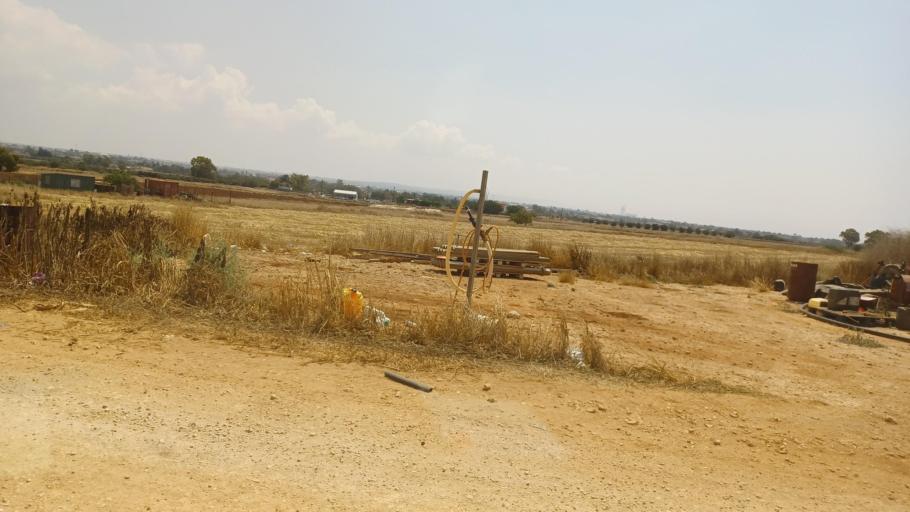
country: CY
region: Ammochostos
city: Liopetri
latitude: 34.9828
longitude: 33.8666
